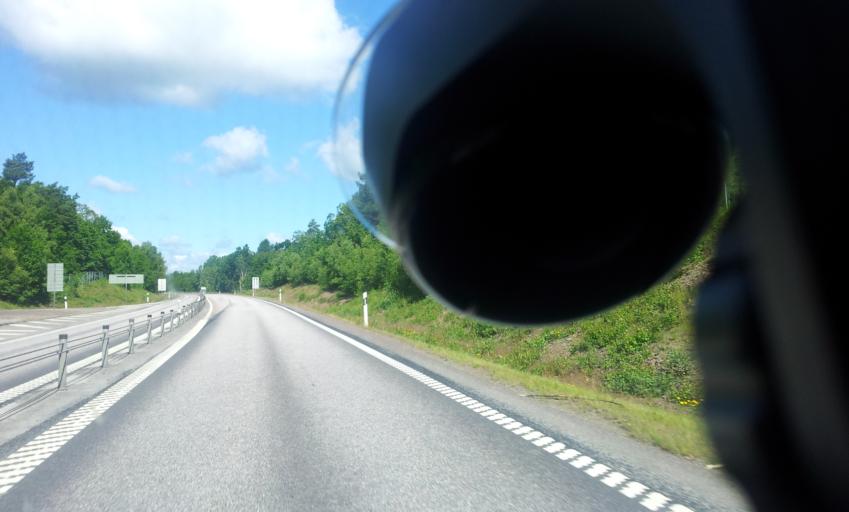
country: SE
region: Kalmar
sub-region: Oskarshamns Kommun
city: Paskallavik
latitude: 57.1515
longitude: 16.4635
